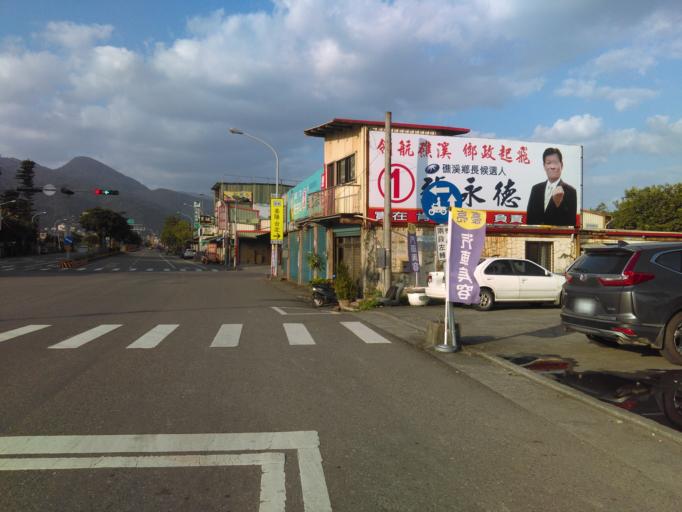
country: TW
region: Taiwan
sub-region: Yilan
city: Yilan
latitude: 24.8088
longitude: 121.7671
